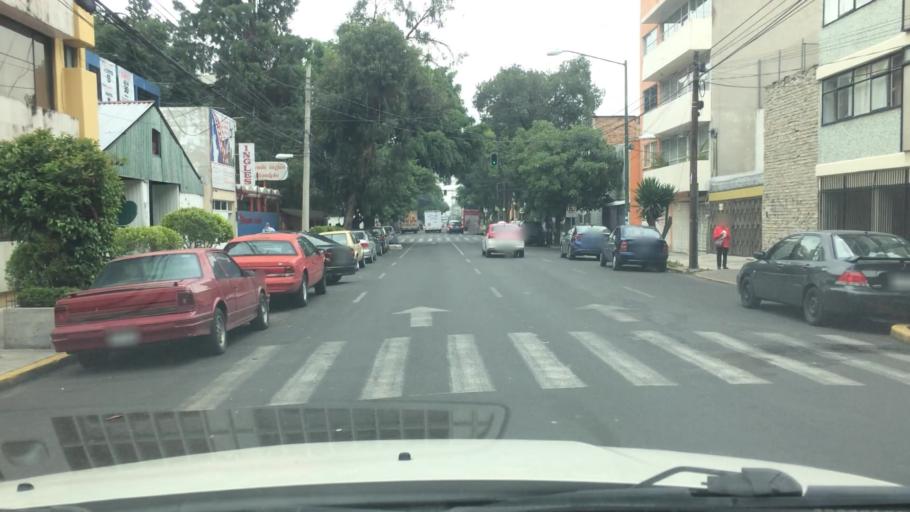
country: MX
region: Mexico City
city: Colonia del Valle
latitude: 19.3688
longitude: -99.1678
